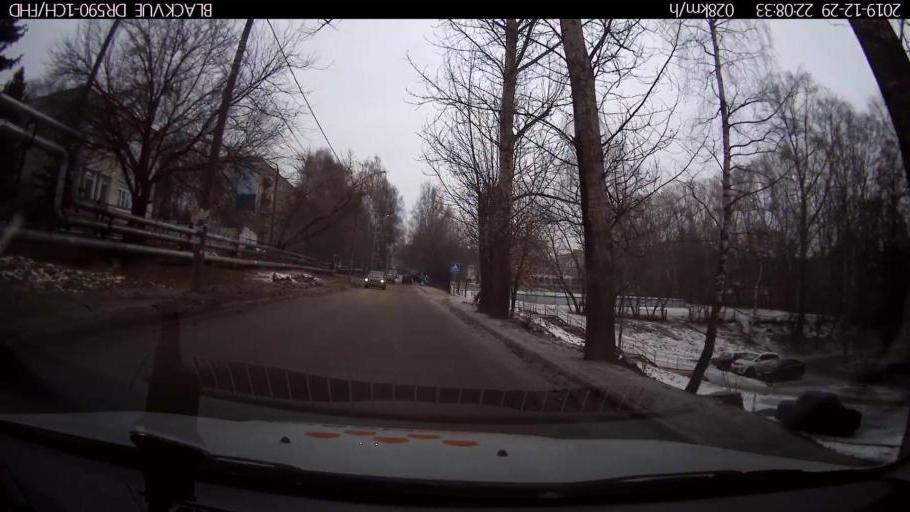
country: RU
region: Nizjnij Novgorod
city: Nizhniy Novgorod
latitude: 56.2304
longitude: 43.9505
